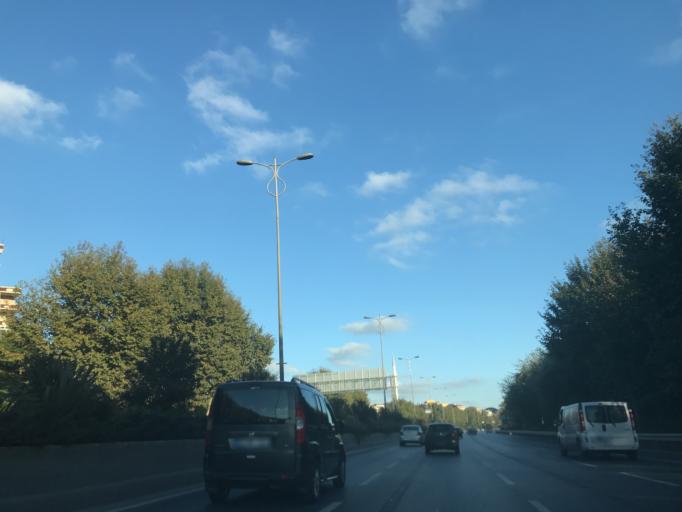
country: TR
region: Istanbul
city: Esenler
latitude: 41.0527
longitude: 28.8677
